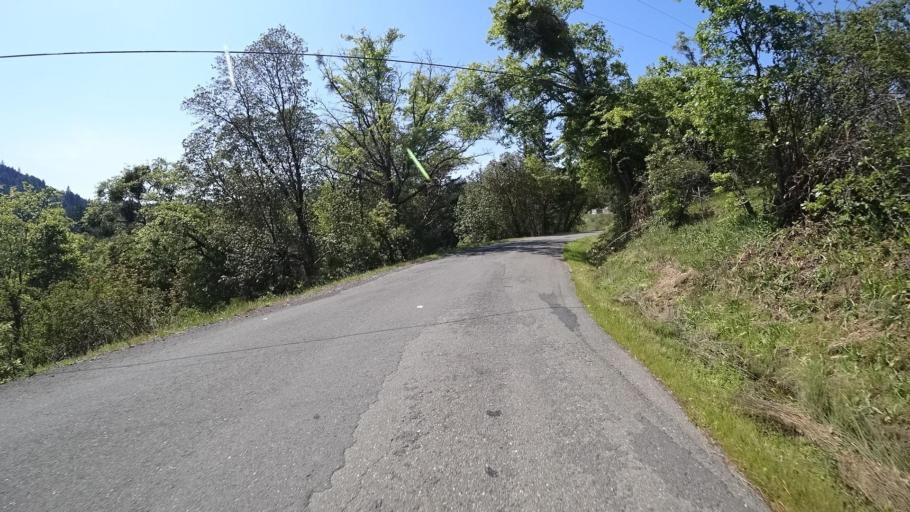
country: US
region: California
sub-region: Humboldt County
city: Redway
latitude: 40.2727
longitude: -123.6283
